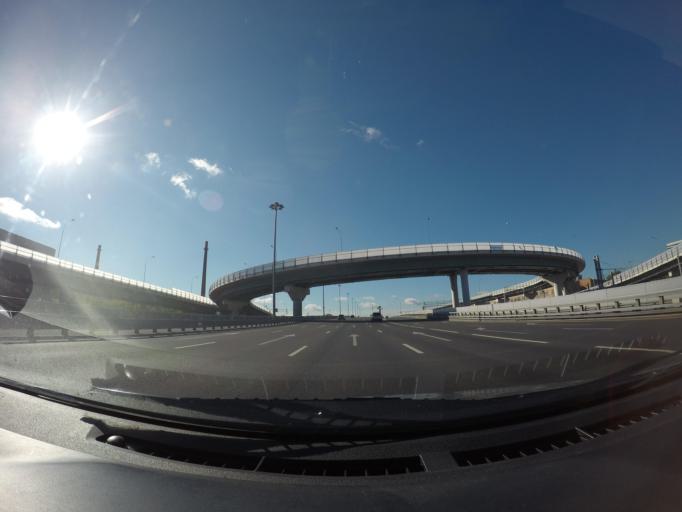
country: RU
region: Moscow
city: Ryazanskiy
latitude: 55.7616
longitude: 37.7475
